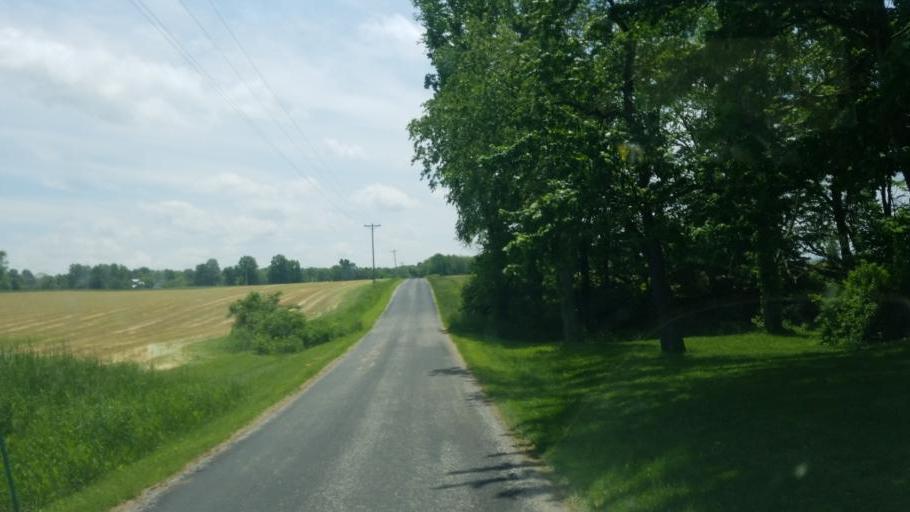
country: US
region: Ohio
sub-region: Ashland County
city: Ashland
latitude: 40.8354
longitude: -82.1938
